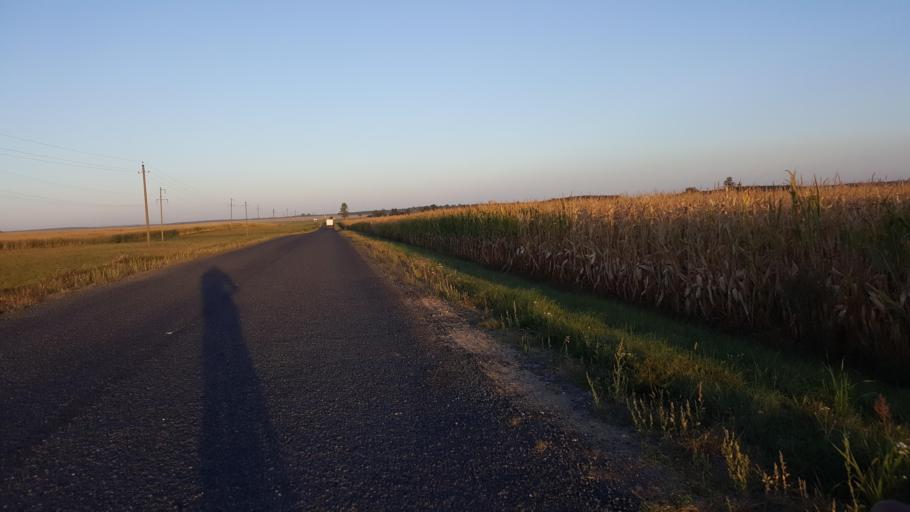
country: BY
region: Brest
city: Charnawchytsy
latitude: 52.2908
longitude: 23.5672
